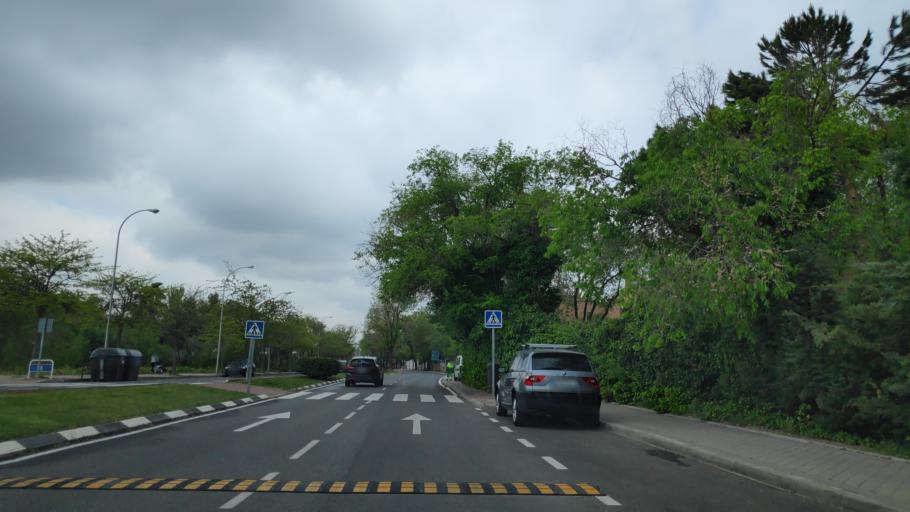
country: ES
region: Madrid
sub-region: Provincia de Madrid
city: Pozuelo de Alarcon
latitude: 40.4598
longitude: -3.7888
